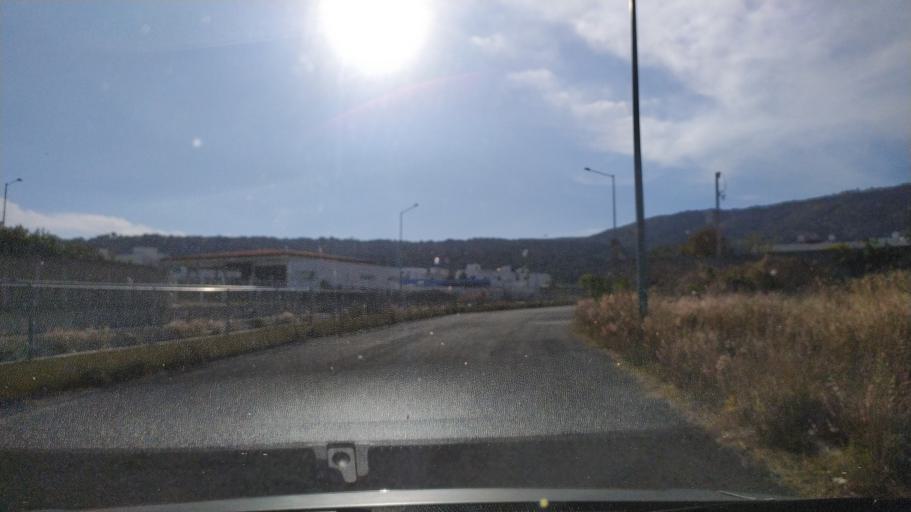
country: MX
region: Jalisco
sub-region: Tlajomulco de Zuniga
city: Palomar
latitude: 20.6299
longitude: -103.4813
